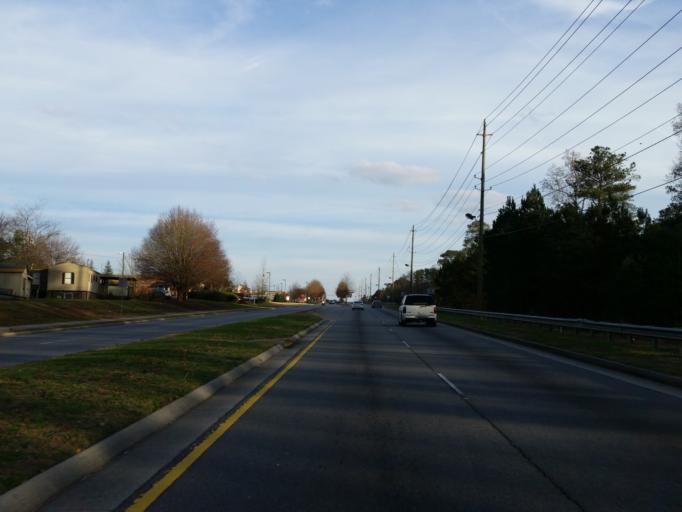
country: US
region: Georgia
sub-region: Cobb County
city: Powder Springs
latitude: 33.8652
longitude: -84.6828
